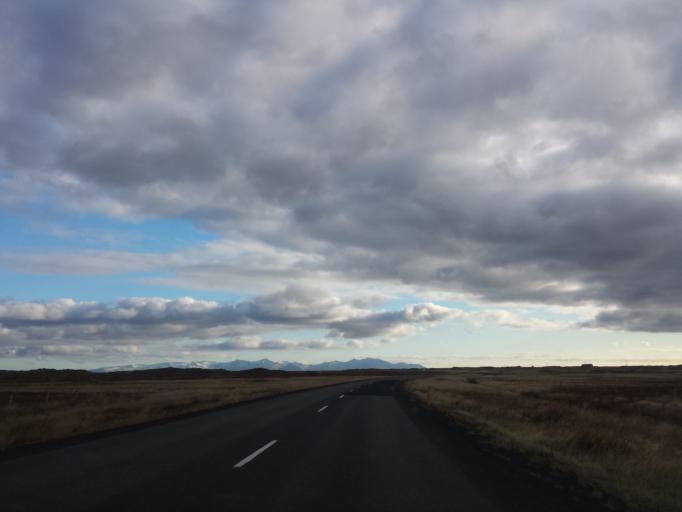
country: IS
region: West
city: Borgarnes
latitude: 64.7116
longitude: -22.1486
